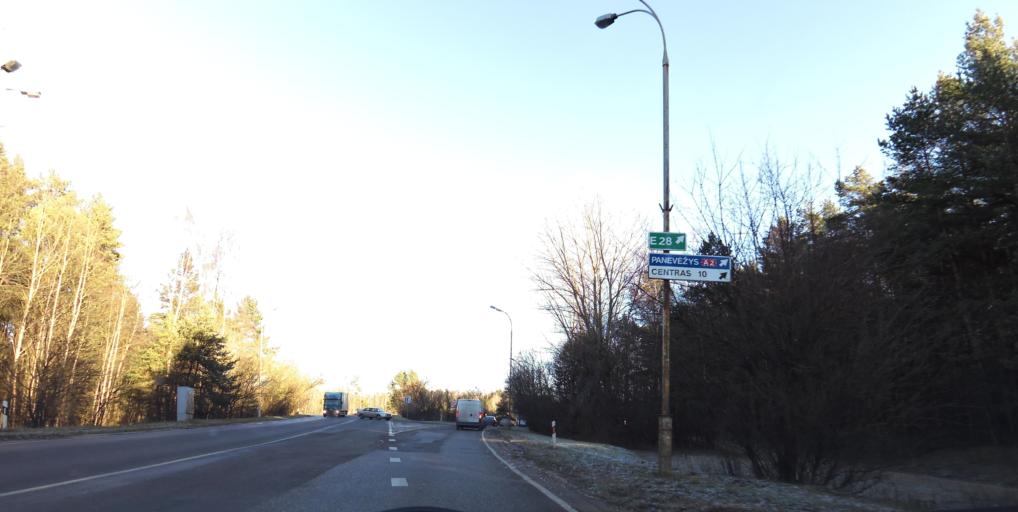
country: LT
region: Vilnius County
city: Lazdynai
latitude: 54.6396
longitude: 25.1795
